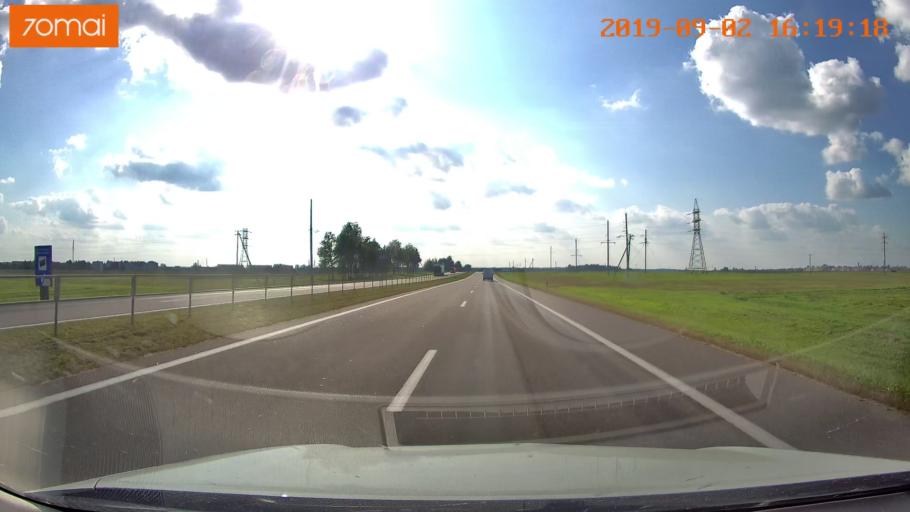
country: BY
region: Minsk
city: Chervyen'
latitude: 53.7265
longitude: 28.4143
